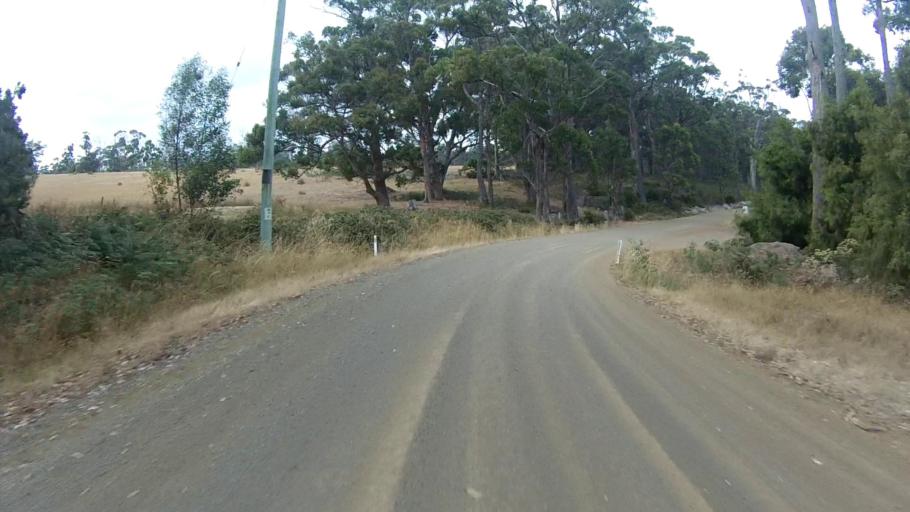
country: AU
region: Tasmania
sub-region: Huon Valley
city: Cygnet
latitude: -43.2380
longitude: 147.0999
